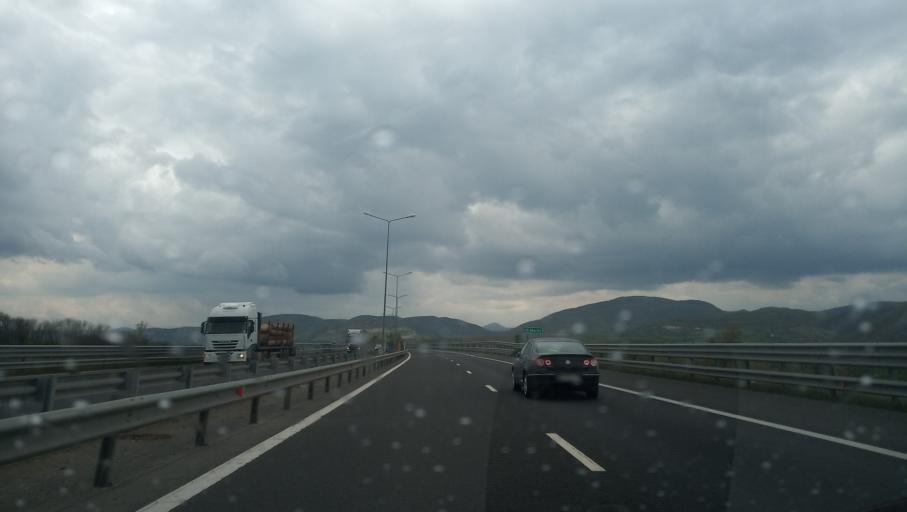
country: RO
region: Hunedoara
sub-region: Oras Simeria
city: Simeria
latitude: 45.8618
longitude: 23.0270
